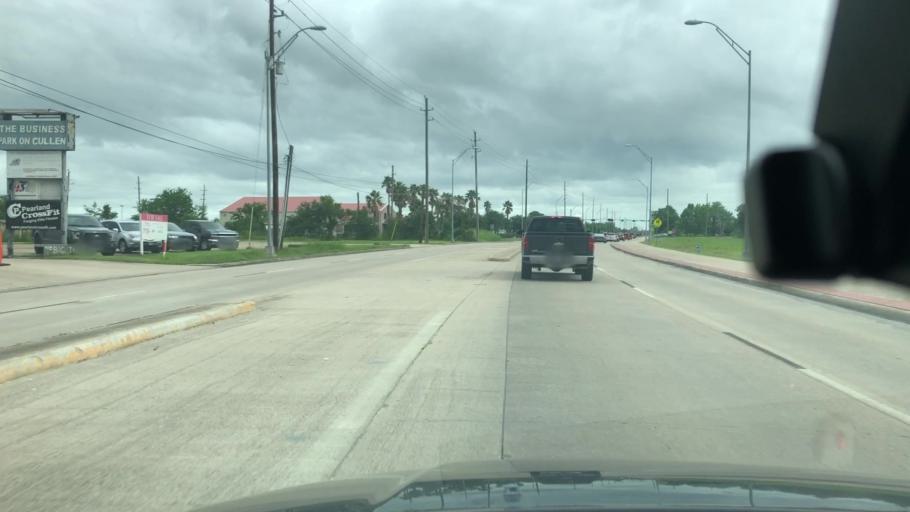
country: US
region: Texas
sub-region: Brazoria County
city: Brookside Village
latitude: 29.5790
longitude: -95.3511
